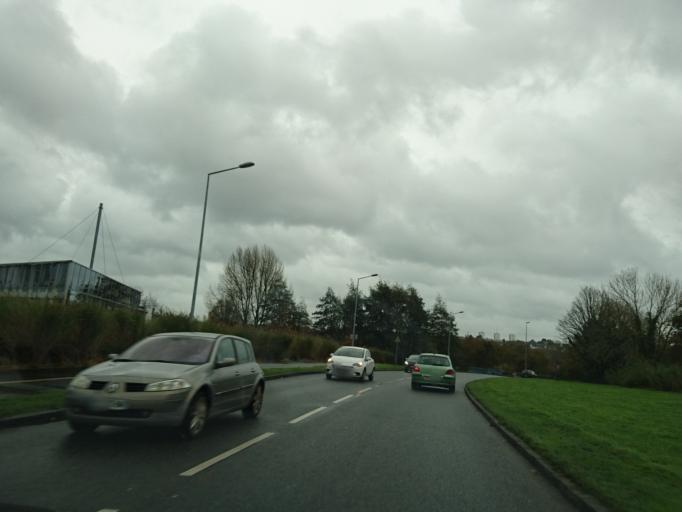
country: FR
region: Brittany
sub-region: Departement du Finistere
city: Bohars
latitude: 48.4064
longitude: -4.5225
